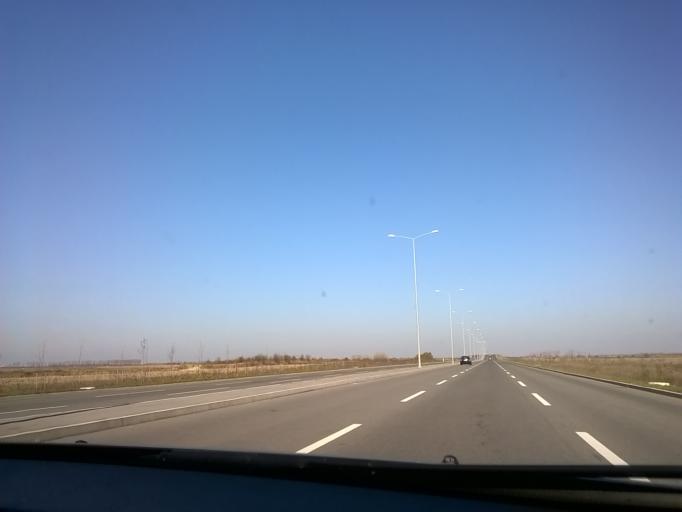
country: RS
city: Ovca
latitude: 44.9014
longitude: 20.5141
